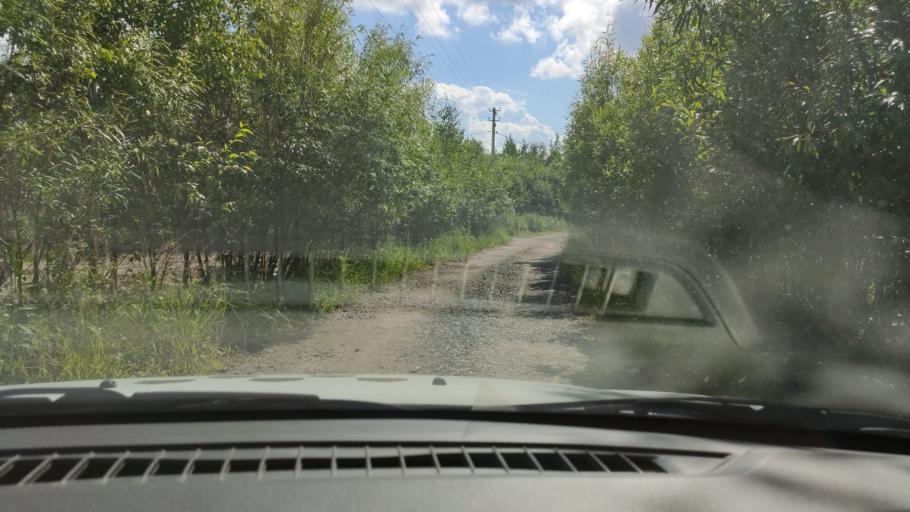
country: RU
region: Perm
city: Kondratovo
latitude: 57.9989
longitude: 56.0430
